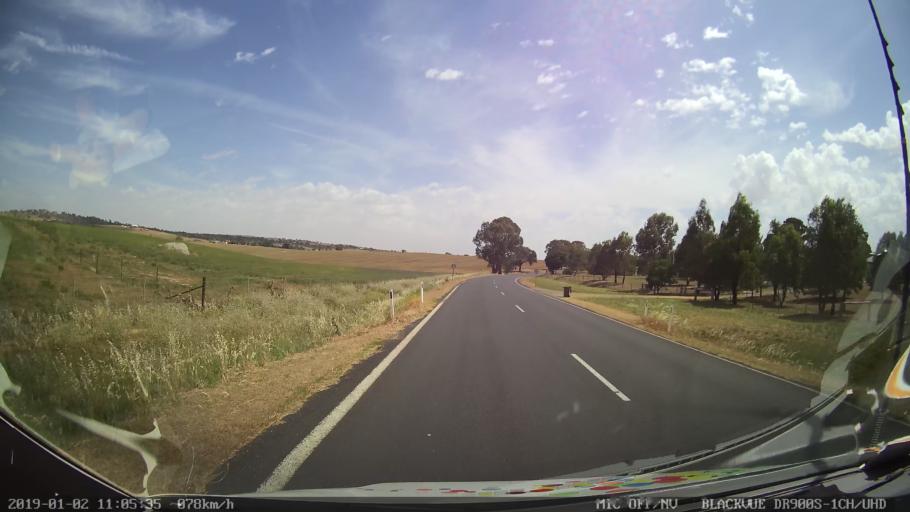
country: AU
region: New South Wales
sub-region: Young
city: Young
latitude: -34.5631
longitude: 148.3538
